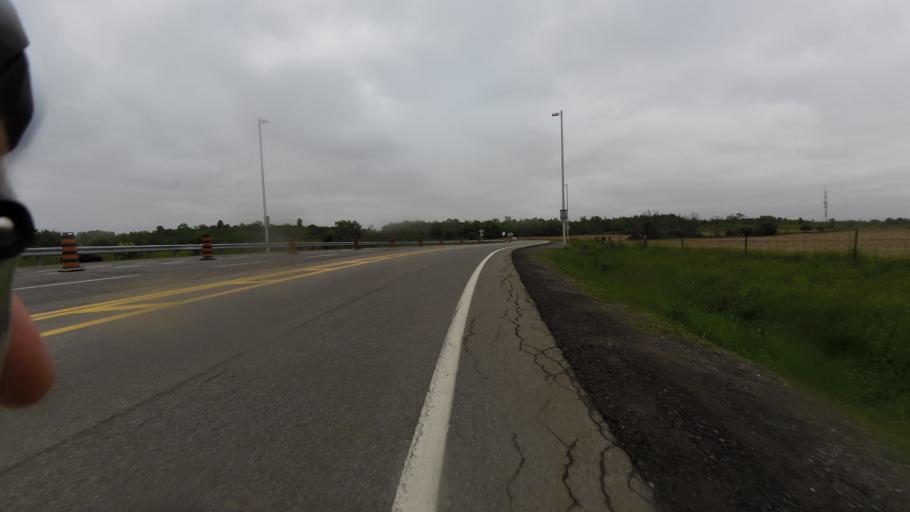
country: CA
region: Ontario
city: Bells Corners
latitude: 45.3144
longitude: -75.8813
